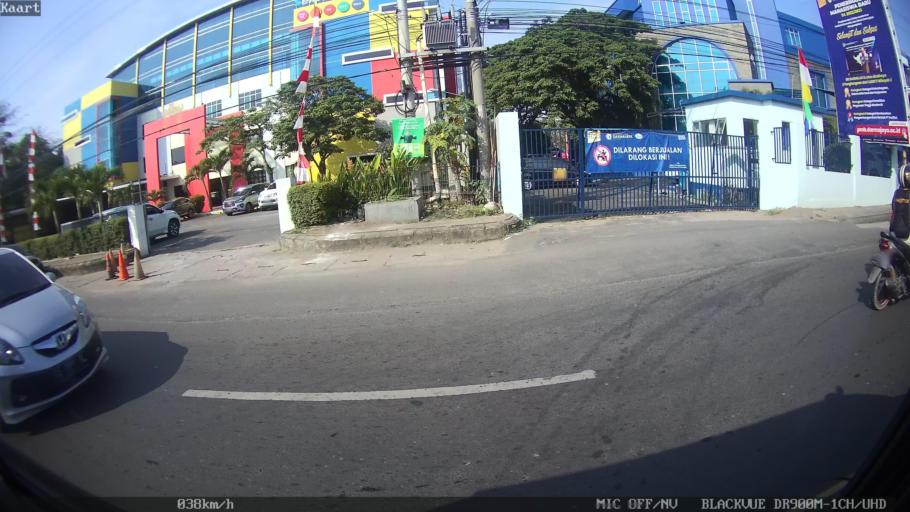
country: ID
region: Lampung
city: Kedaton
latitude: -5.3778
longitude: 105.2509
